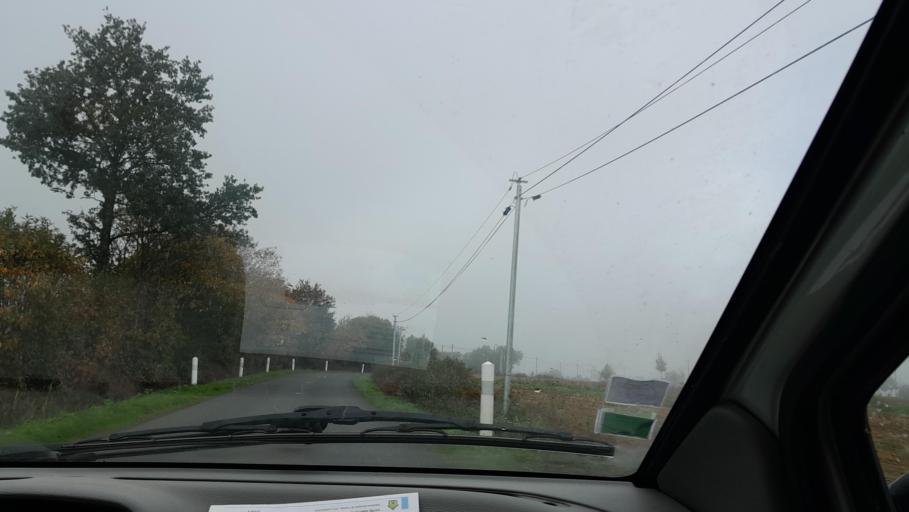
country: FR
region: Pays de la Loire
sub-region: Departement de la Mayenne
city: Saint-Pierre-la-Cour
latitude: 48.1388
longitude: -1.0257
